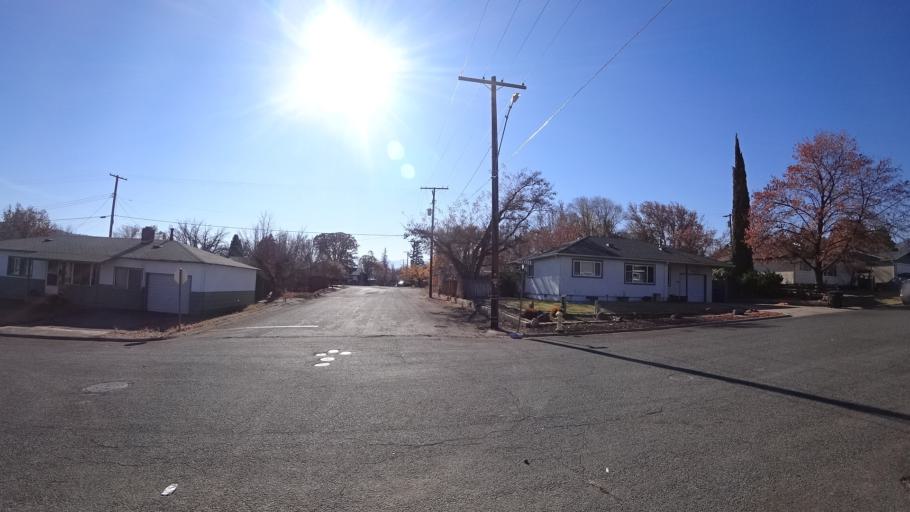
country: US
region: California
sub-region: Siskiyou County
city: Yreka
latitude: 41.7408
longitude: -122.6432
